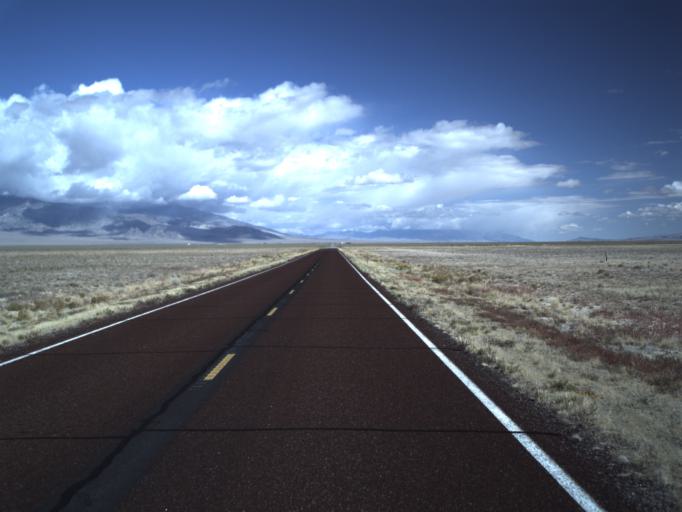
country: US
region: Nevada
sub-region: White Pine County
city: McGill
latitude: 38.9802
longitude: -114.0341
